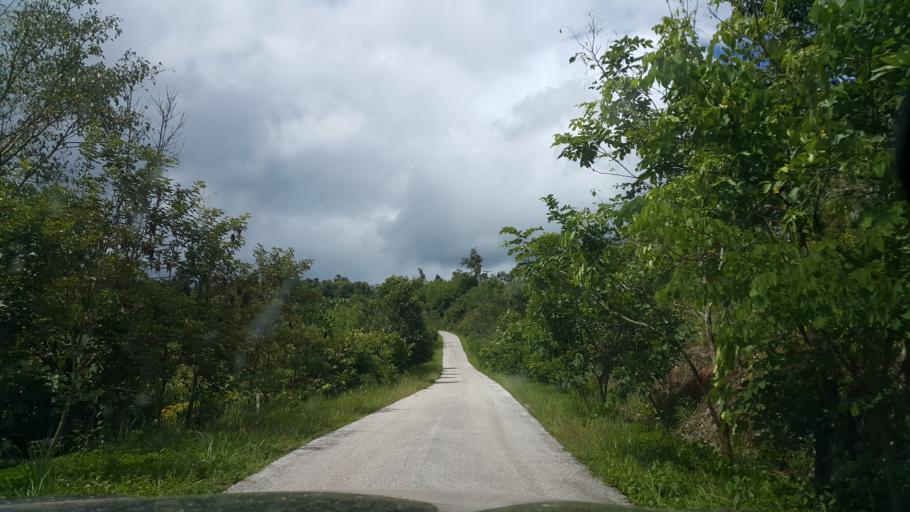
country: TH
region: Loei
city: Na Haeo
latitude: 17.6015
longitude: 100.9028
